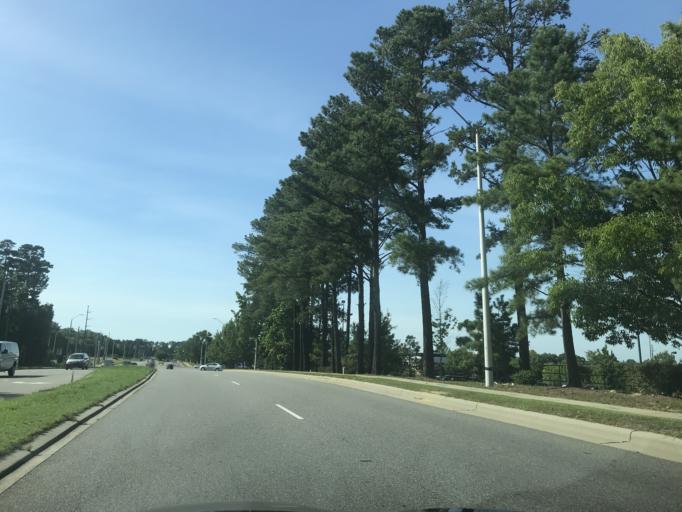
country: US
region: North Carolina
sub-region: Wake County
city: Garner
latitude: 35.6875
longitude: -78.5810
